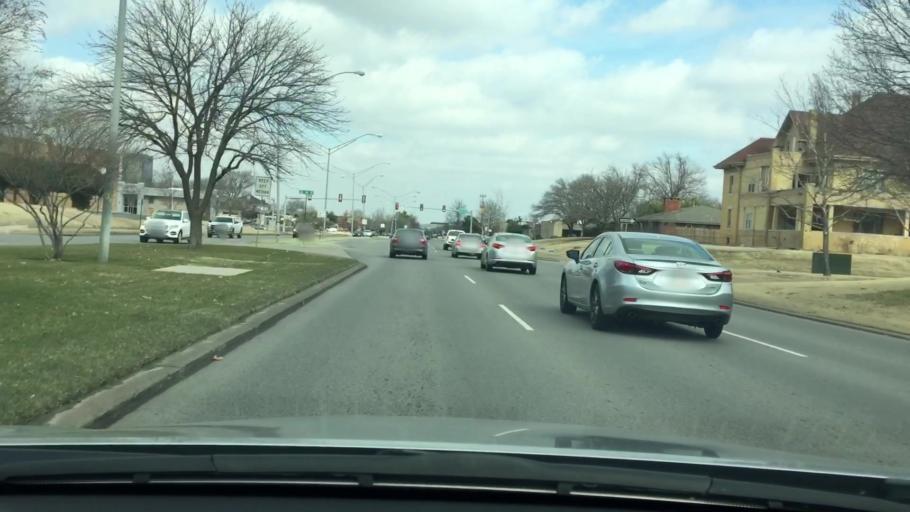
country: US
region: Oklahoma
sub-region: Oklahoma County
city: Nichols Hills
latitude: 35.5099
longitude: -97.5343
